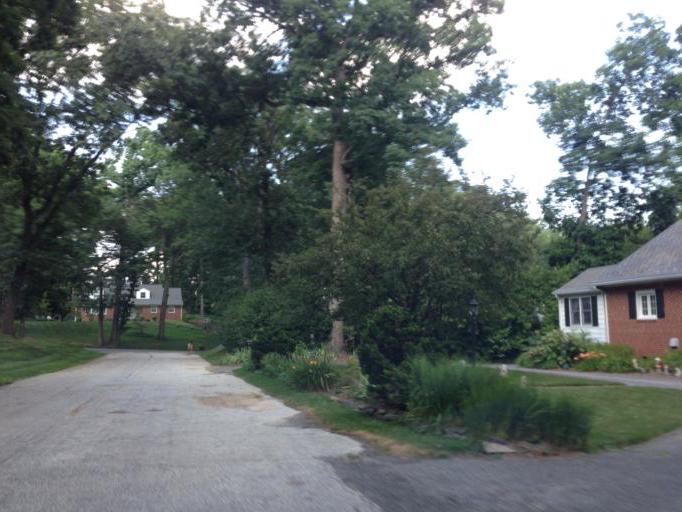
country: US
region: Maryland
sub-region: Baltimore County
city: Towson
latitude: 39.3920
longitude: -76.5886
